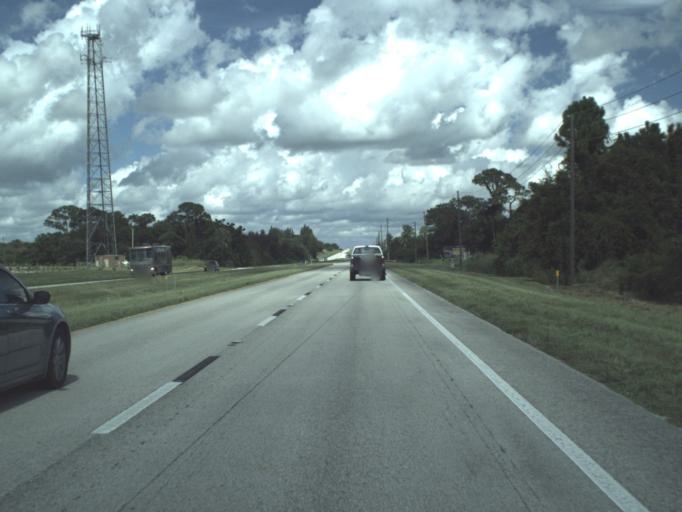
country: US
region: Florida
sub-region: Highlands County
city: Lake Placid
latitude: 27.2485
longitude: -81.3382
